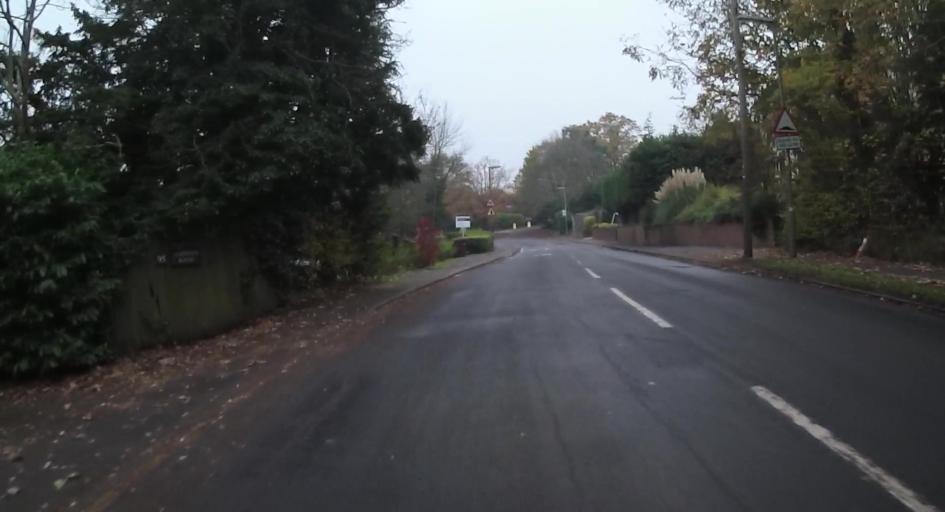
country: GB
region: England
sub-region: Surrey
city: Farnham
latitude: 51.1948
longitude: -0.8140
